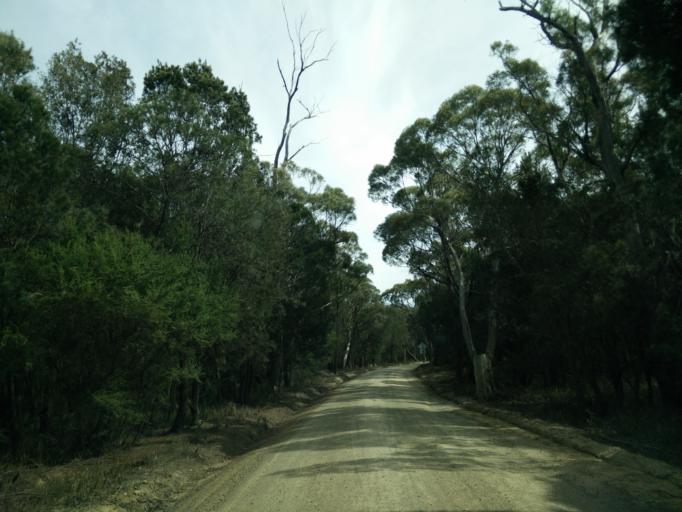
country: AU
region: Tasmania
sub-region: Break O'Day
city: St Helens
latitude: -42.0010
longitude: 148.2728
